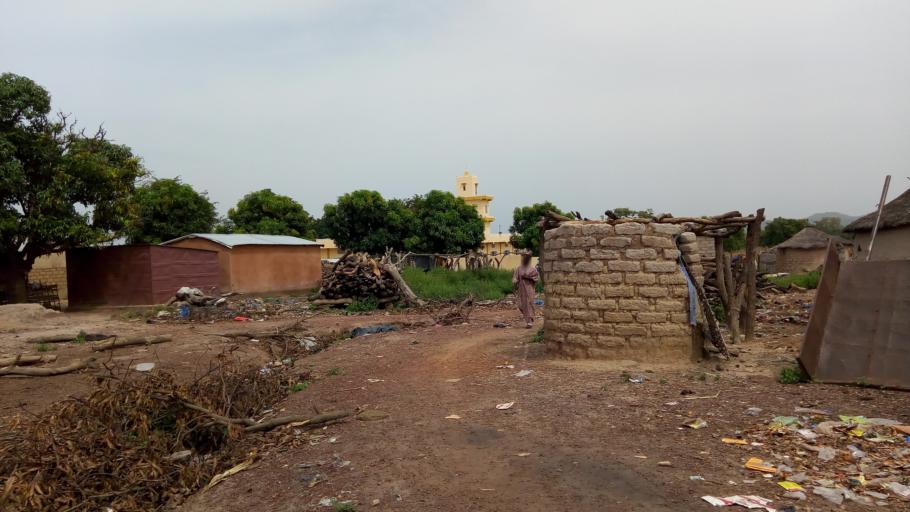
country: ML
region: Koulikoro
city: Kangaba
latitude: 11.4956
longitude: -8.5487
